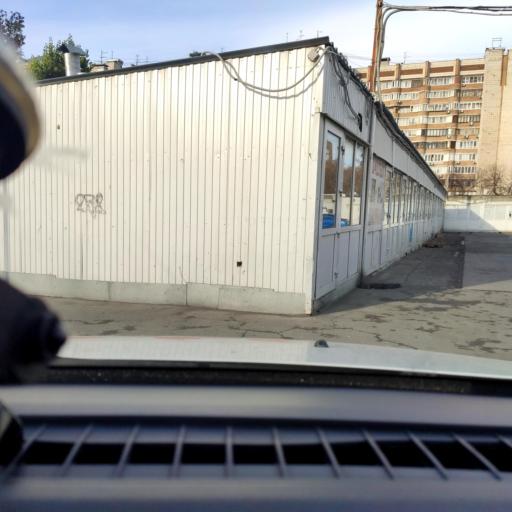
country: RU
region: Samara
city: Samara
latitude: 53.1923
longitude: 50.1234
